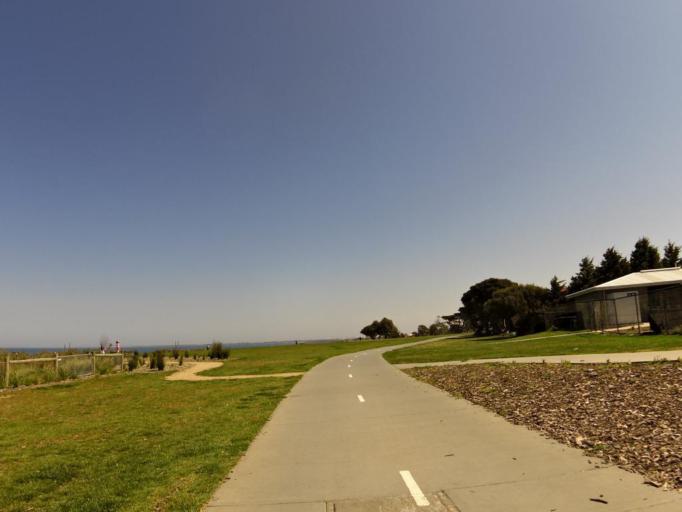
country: AU
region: Victoria
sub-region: Hobsons Bay
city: Williamstown
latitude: -37.8721
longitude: 144.9027
